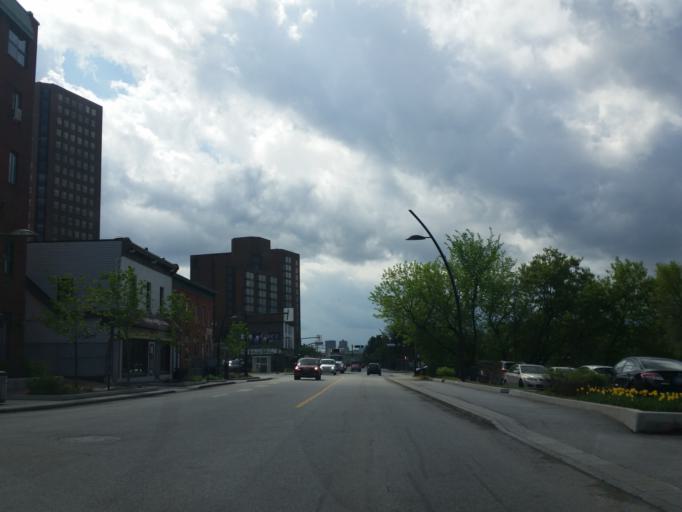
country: CA
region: Ontario
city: Ottawa
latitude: 45.4272
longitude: -75.7246
